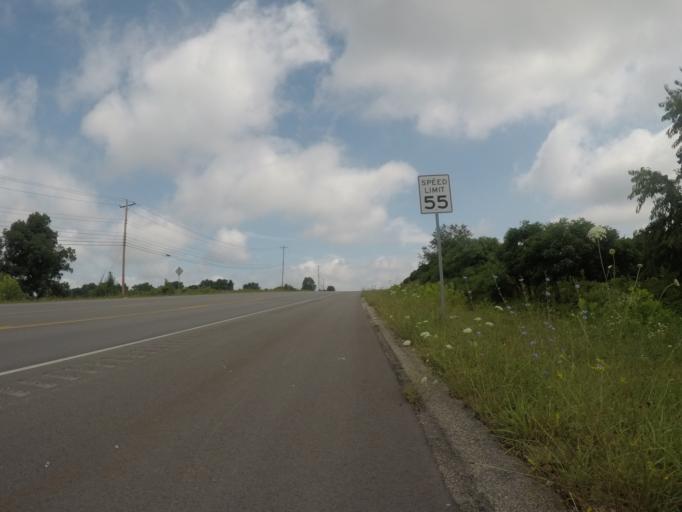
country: US
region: Kentucky
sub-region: Boyd County
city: Meads
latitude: 38.3599
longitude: -82.6976
